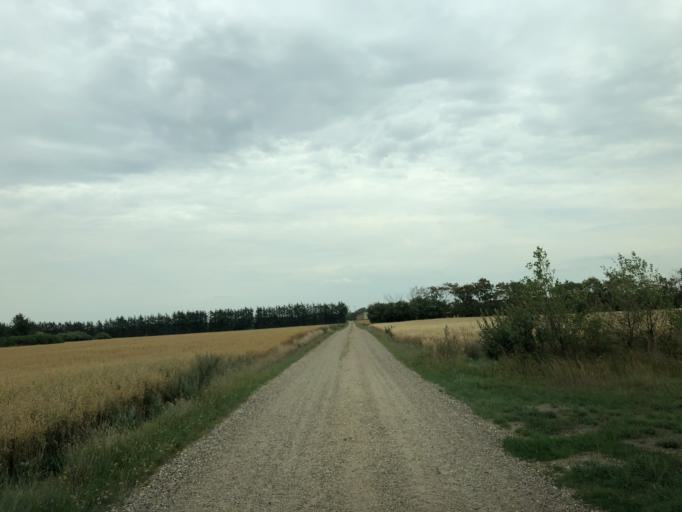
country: DK
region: Central Jutland
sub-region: Holstebro Kommune
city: Ulfborg
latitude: 56.2392
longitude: 8.3640
